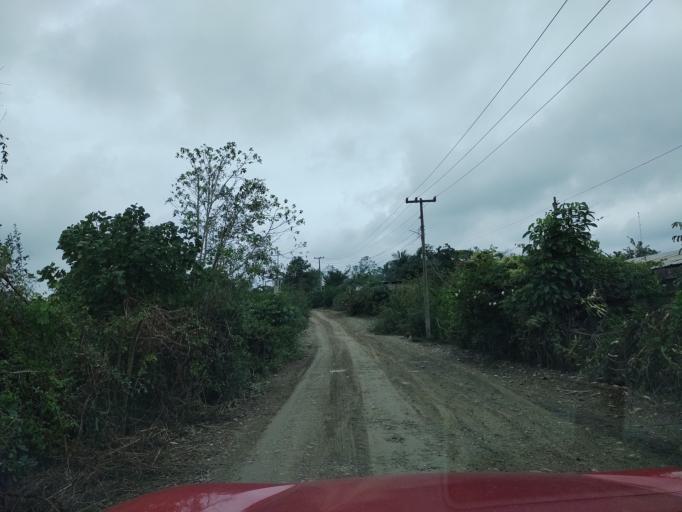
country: MX
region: Veracruz
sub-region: Coatzintla
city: Manuel Maria Contreras
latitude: 20.4095
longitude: -97.4572
